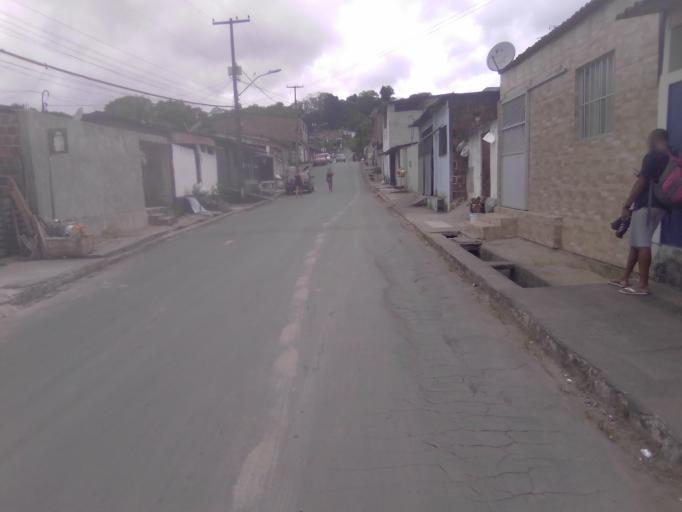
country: BR
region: Pernambuco
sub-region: Jaboatao Dos Guararapes
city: Jaboatao dos Guararapes
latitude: -8.0661
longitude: -35.0018
